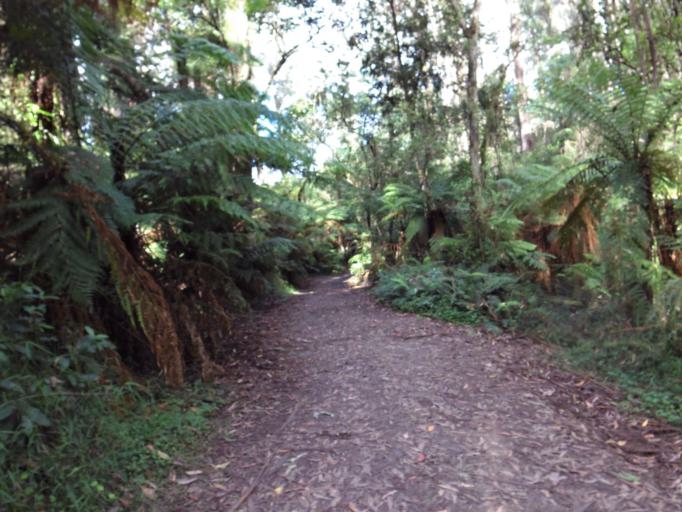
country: AU
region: Victoria
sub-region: Yarra Ranges
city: Belgrave
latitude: -37.8856
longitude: 145.3514
